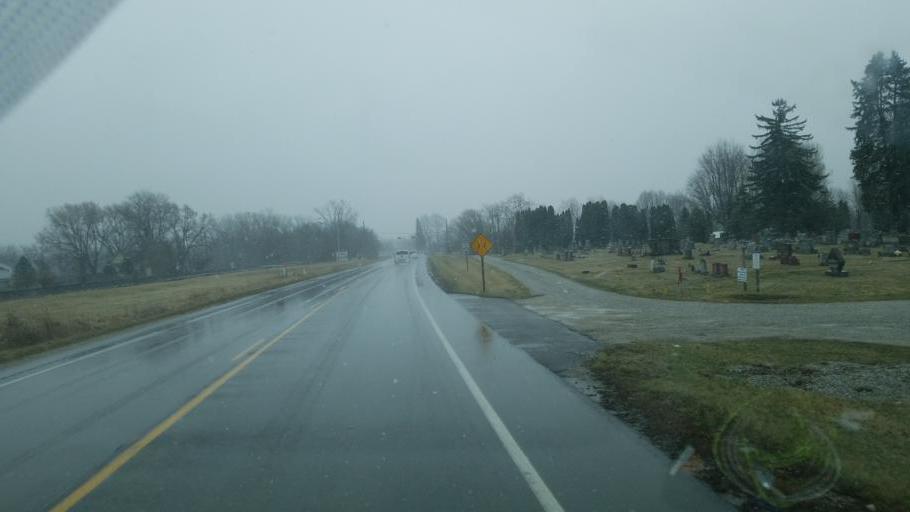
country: US
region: Indiana
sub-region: Wabash County
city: Mount Vernon
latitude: 40.6758
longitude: -85.7272
